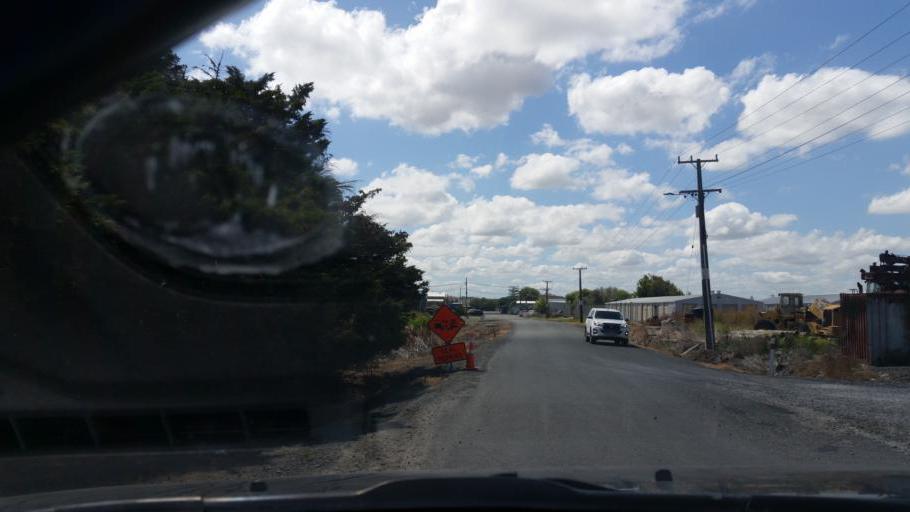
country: NZ
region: Northland
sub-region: Kaipara District
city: Dargaville
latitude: -35.9443
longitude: 173.8606
